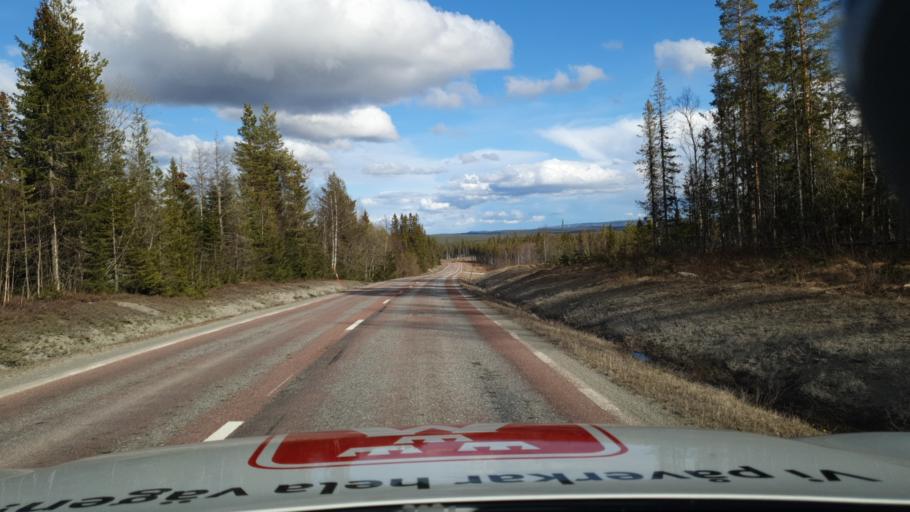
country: SE
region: Jaemtland
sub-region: Bergs Kommun
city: Hoverberg
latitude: 62.4753
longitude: 14.1977
